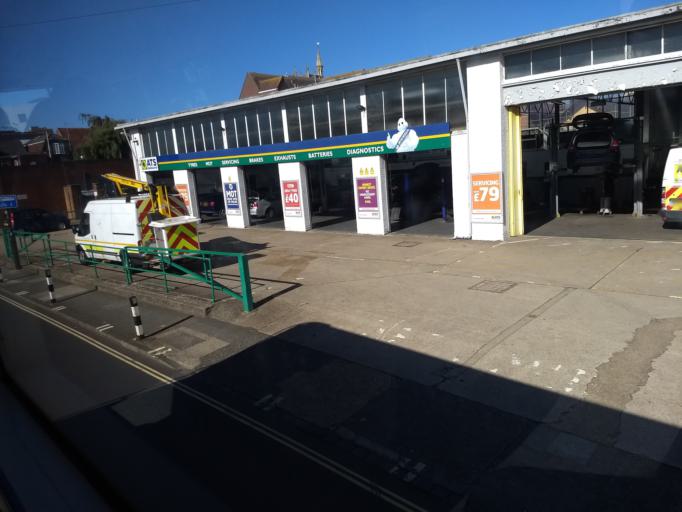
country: GB
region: England
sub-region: Isle of Wight
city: Newport
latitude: 50.6989
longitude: -1.2919
